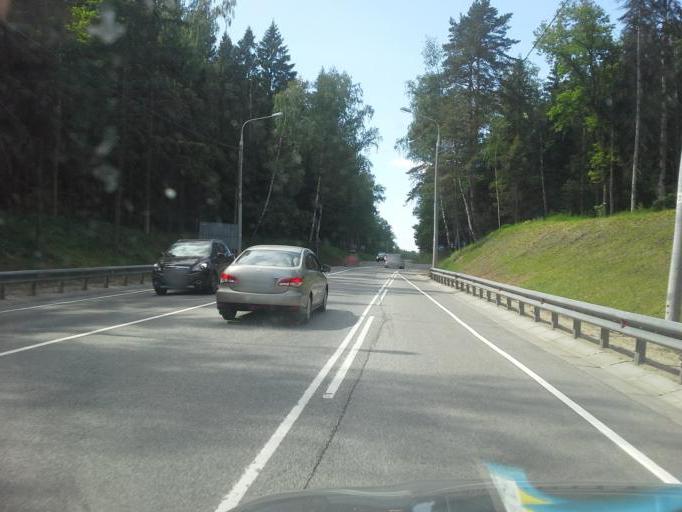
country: RU
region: Moskovskaya
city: Odintsovo
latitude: 55.6916
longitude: 37.2400
